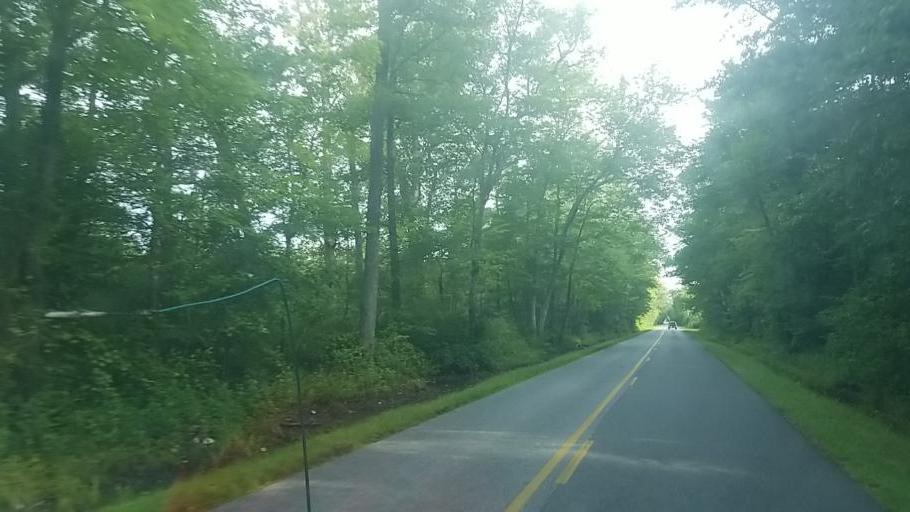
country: US
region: Maryland
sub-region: Worcester County
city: West Ocean City
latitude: 38.3307
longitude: -75.1559
